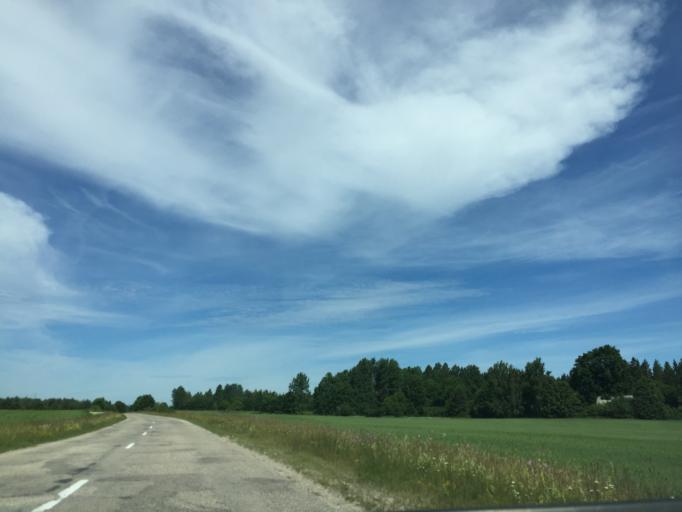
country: LV
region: Dundaga
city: Dundaga
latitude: 57.5427
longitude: 22.3266
